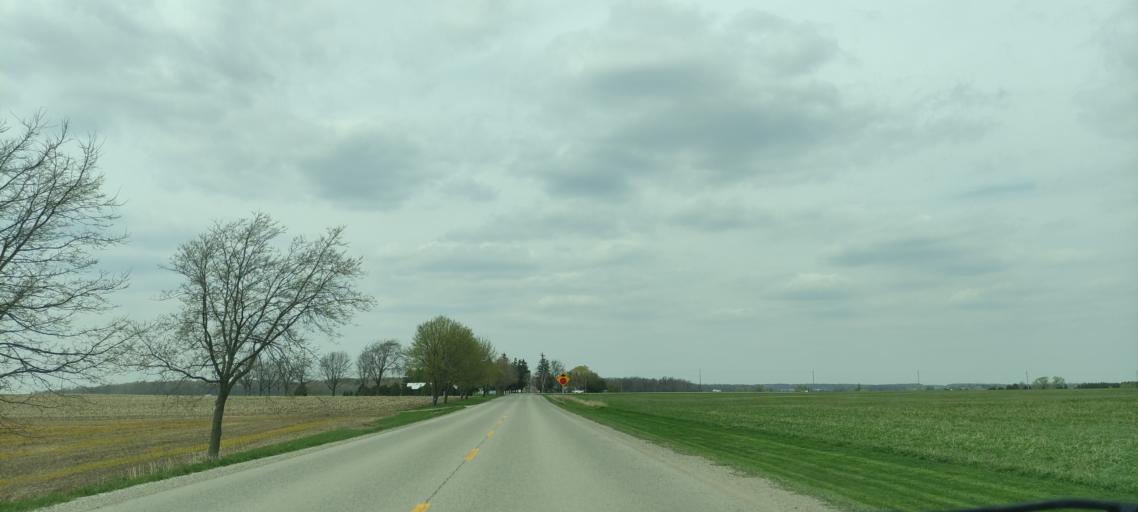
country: CA
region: Ontario
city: Stratford
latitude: 43.3309
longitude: -80.7910
